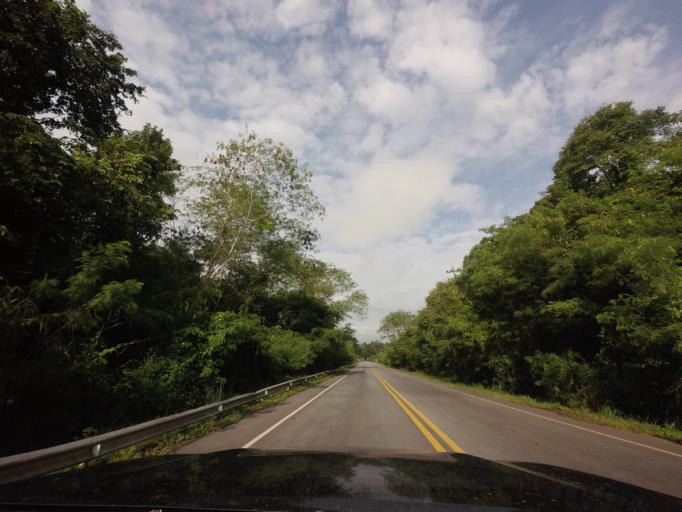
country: TH
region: Nong Khai
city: Pho Tak
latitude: 17.8036
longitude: 102.3184
